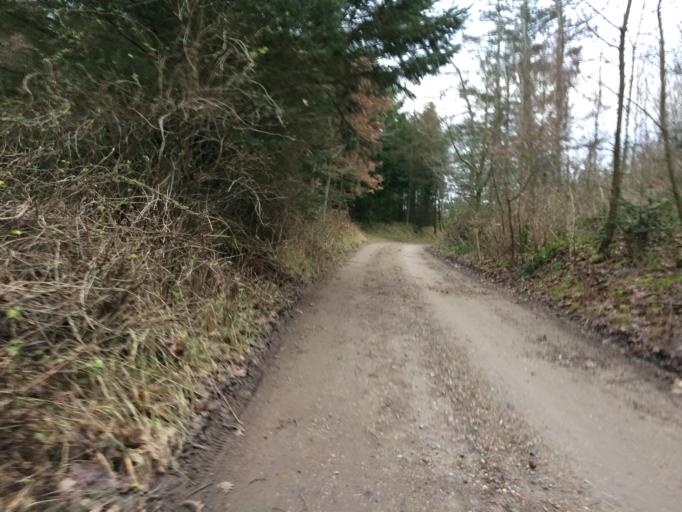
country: DK
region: Central Jutland
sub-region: Holstebro Kommune
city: Ulfborg
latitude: 56.2645
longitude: 8.2471
